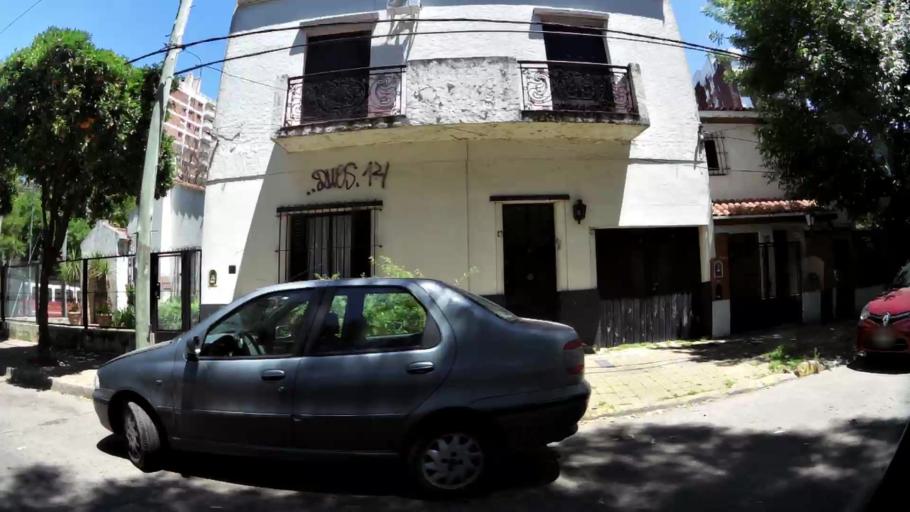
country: AR
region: Buenos Aires
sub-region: Partido de San Isidro
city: San Isidro
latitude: -34.4759
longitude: -58.5097
